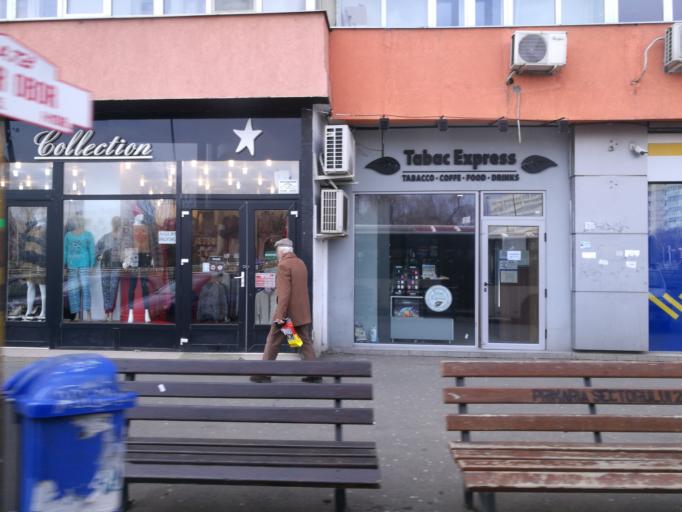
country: RO
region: Bucuresti
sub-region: Municipiul Bucuresti
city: Bucharest
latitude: 44.4483
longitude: 26.1250
